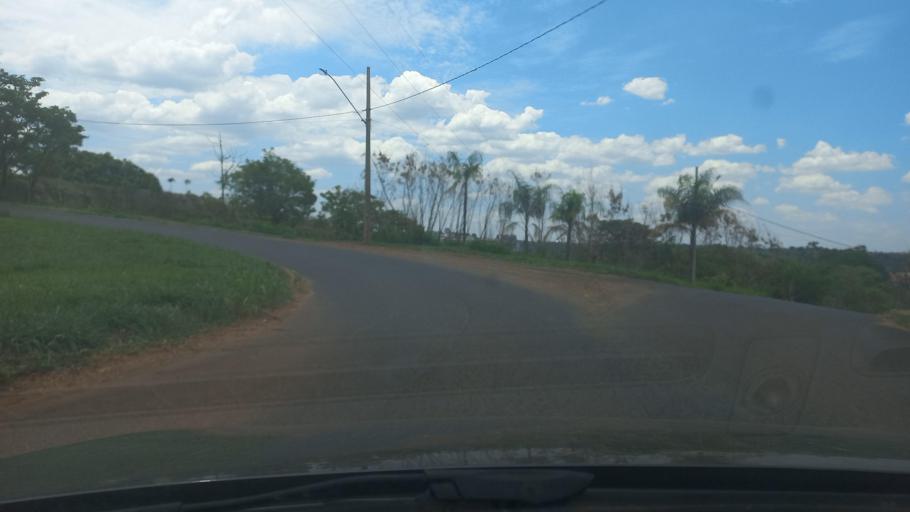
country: BR
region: Minas Gerais
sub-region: Uberaba
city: Uberaba
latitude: -19.7347
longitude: -47.9754
